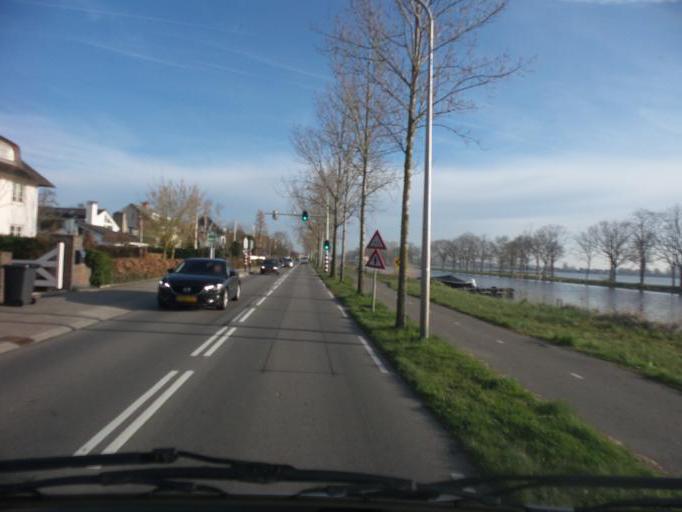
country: NL
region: South Holland
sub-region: Bodegraven-Reeuwijk
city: Reeuwijk
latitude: 52.0315
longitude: 4.7196
